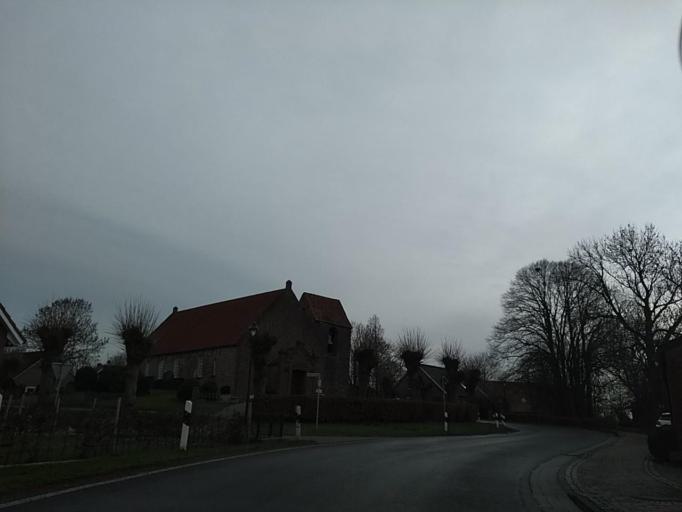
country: DE
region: Lower Saxony
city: Jemgum
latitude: 53.2901
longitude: 7.3575
